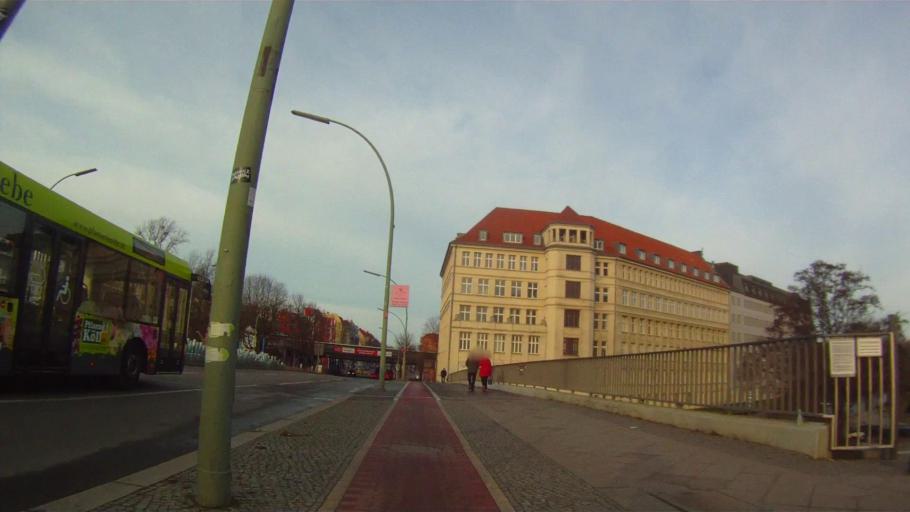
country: DE
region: Berlin
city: Treptow Bezirk
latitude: 52.4729
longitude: 13.4581
